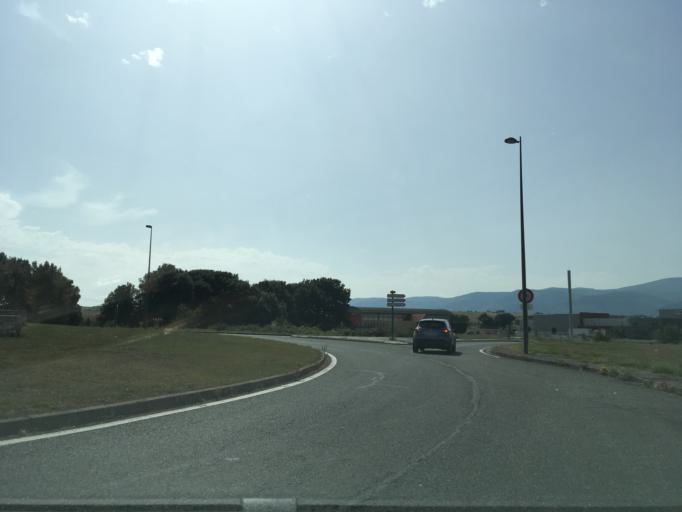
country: FR
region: Midi-Pyrenees
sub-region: Departement du Tarn
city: Lagarrigue
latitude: 43.5564
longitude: 2.2776
